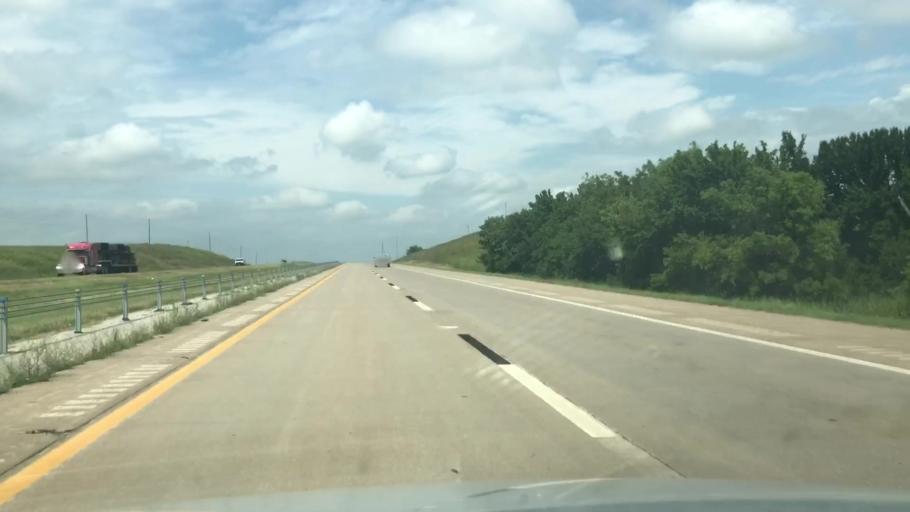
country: US
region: Oklahoma
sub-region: Osage County
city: Skiatook
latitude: 36.4752
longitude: -95.9200
